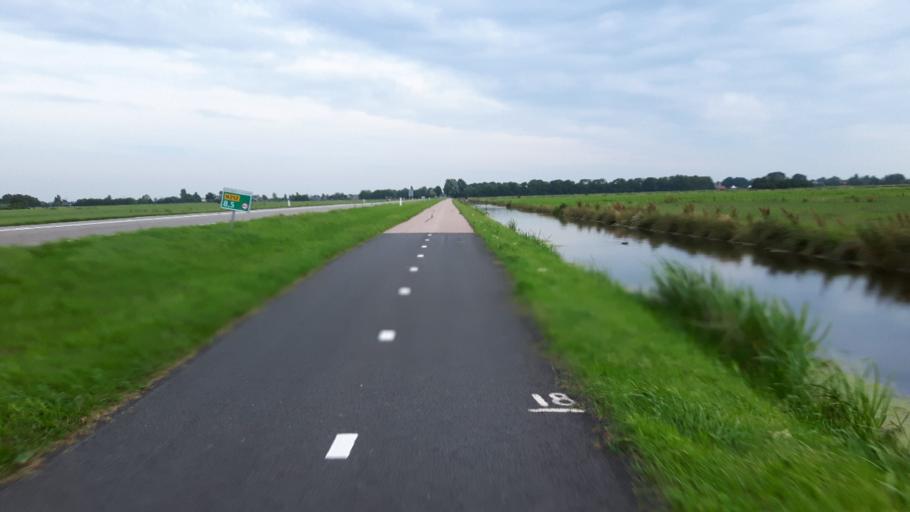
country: NL
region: Utrecht
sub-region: Gemeente Woerden
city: Woerden
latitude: 52.1410
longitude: 4.9116
